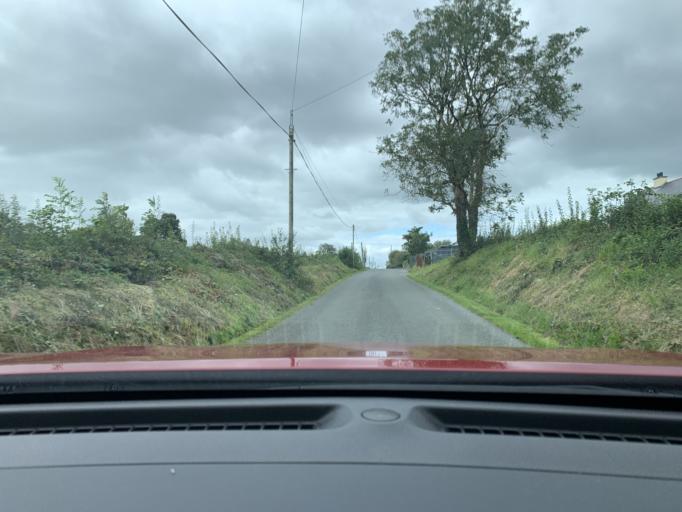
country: IE
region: Connaught
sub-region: Sligo
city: Collooney
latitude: 54.1761
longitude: -8.4416
